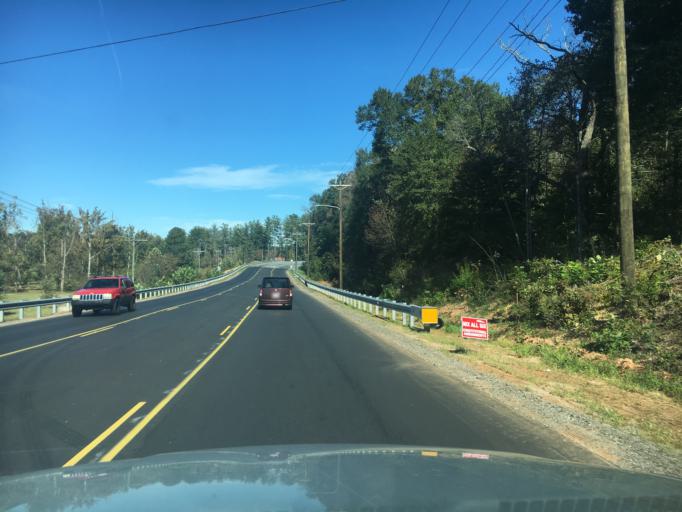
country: US
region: North Carolina
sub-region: Burke County
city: Morganton
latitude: 35.7566
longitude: -81.7029
